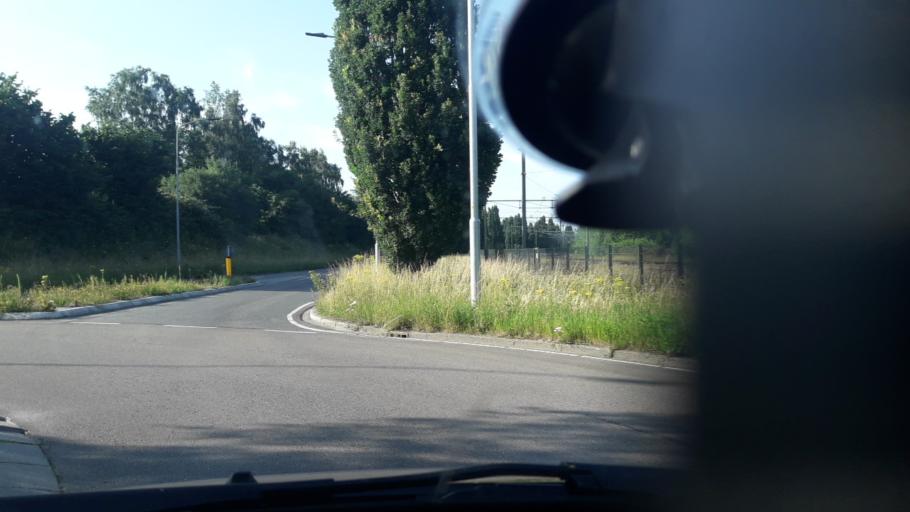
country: NL
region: Gelderland
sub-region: Gemeente Harderwijk
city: Harderwijk
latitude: 52.3318
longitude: 5.6103
